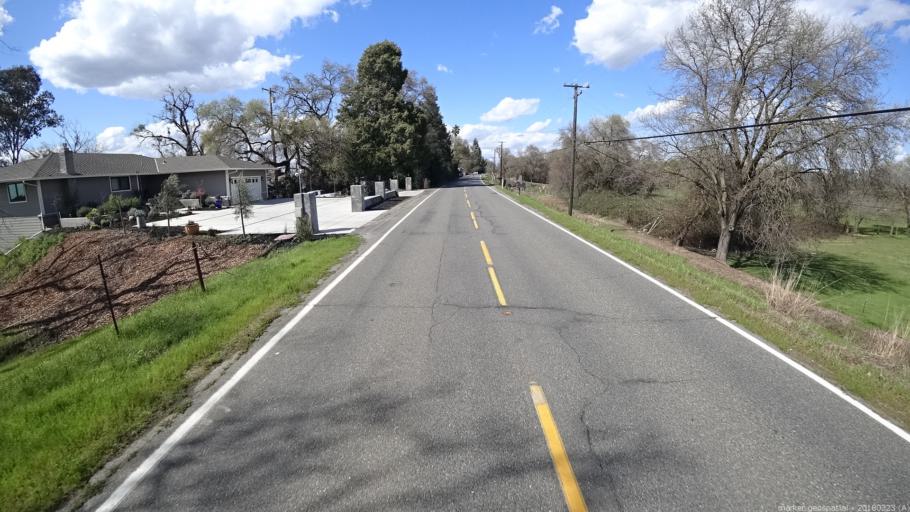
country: US
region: California
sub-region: Yolo County
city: West Sacramento
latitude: 38.6090
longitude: -121.5569
